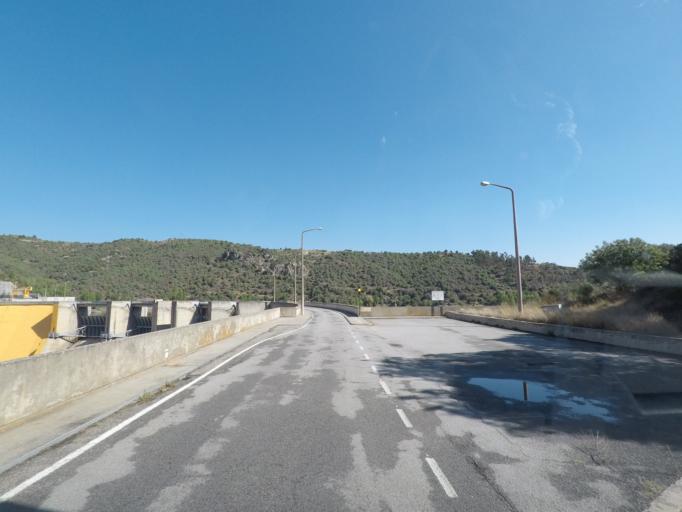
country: ES
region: Castille and Leon
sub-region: Provincia de Salamanca
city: Villarino de los Aires
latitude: 41.2995
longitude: -6.4697
